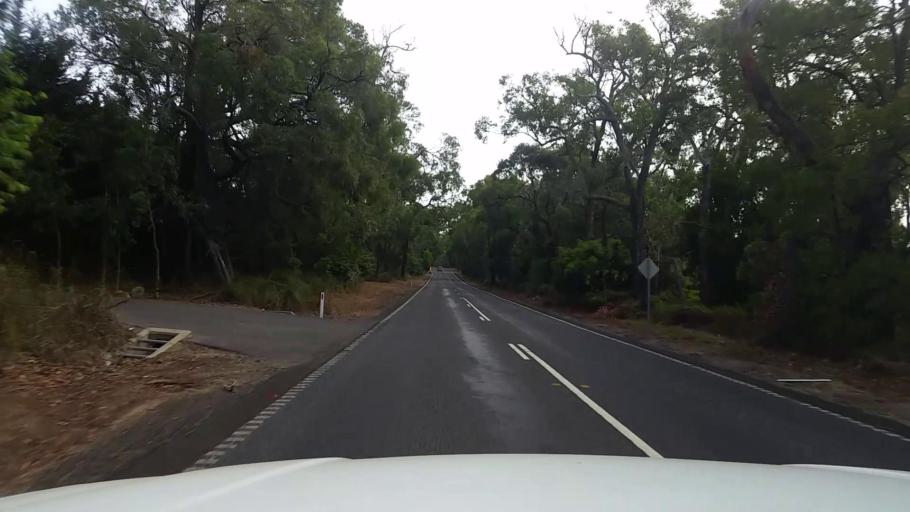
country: AU
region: Victoria
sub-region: Mornington Peninsula
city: Balnarring
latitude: -38.3304
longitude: 145.0941
